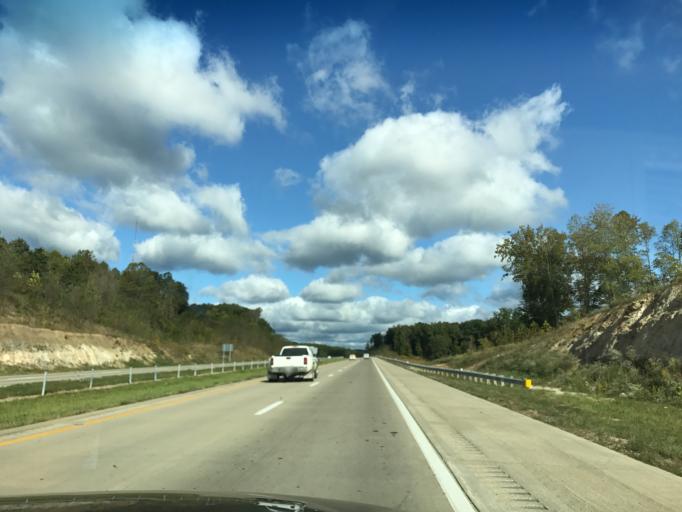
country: US
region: Ohio
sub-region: Athens County
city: Nelsonville
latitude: 39.4579
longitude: -82.2146
